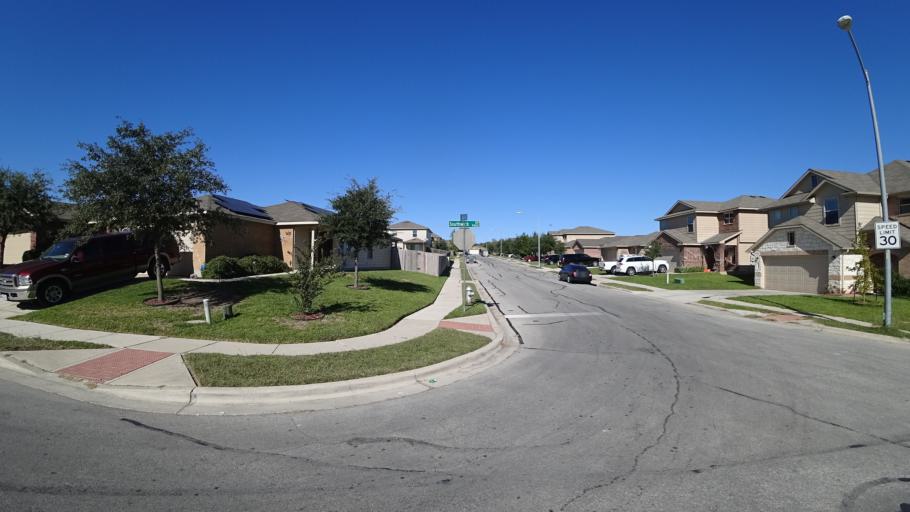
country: US
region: Texas
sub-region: Travis County
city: Hornsby Bend
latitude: 30.2787
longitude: -97.6282
